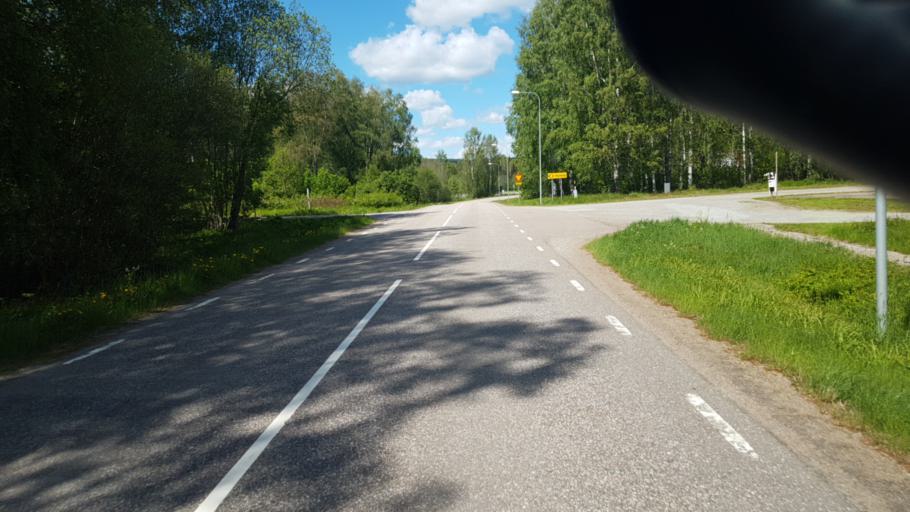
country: SE
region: Vaermland
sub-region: Arvika Kommun
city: Arvika
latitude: 59.6619
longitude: 12.8843
